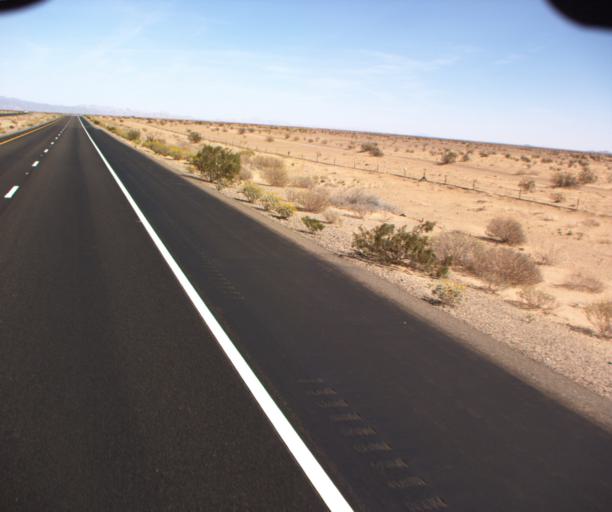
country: US
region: Arizona
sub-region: Yuma County
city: Somerton
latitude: 32.4951
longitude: -114.5864
